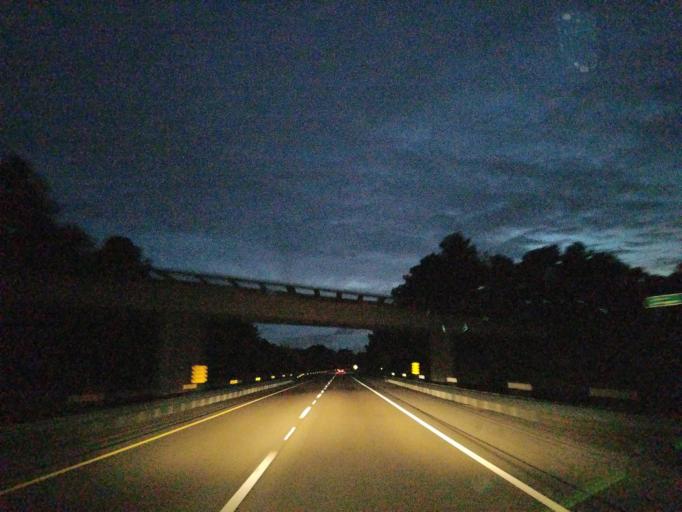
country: US
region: Mississippi
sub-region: Jones County
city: Laurel
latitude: 31.7221
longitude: -89.1038
